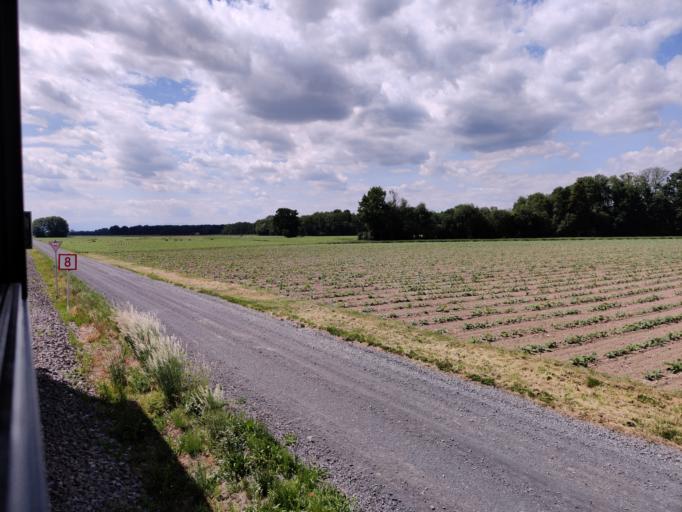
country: AT
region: Styria
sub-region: Politischer Bezirk Suedoststeiermark
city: Mureck
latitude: 46.7116
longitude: 15.7643
